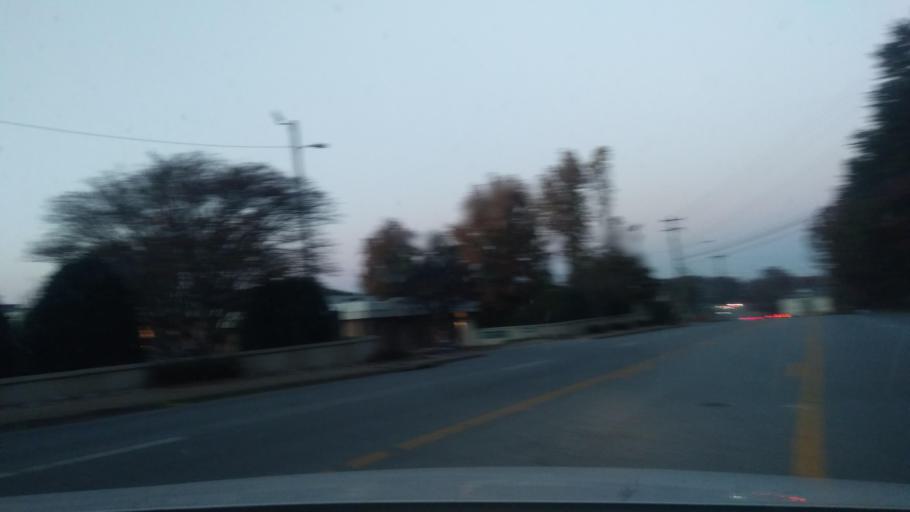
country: US
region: North Carolina
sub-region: Guilford County
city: Jamestown
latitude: 36.0642
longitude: -79.9064
